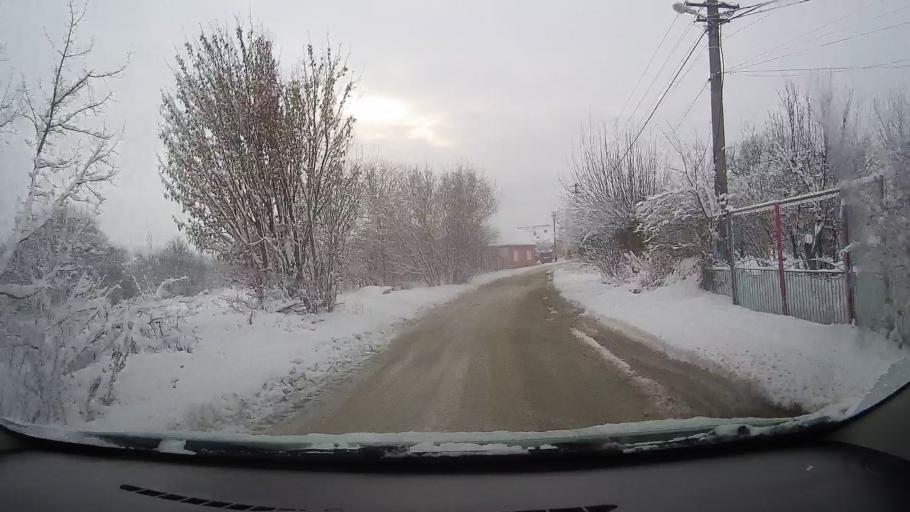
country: RO
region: Alba
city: Vurpar
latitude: 45.9804
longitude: 23.4818
